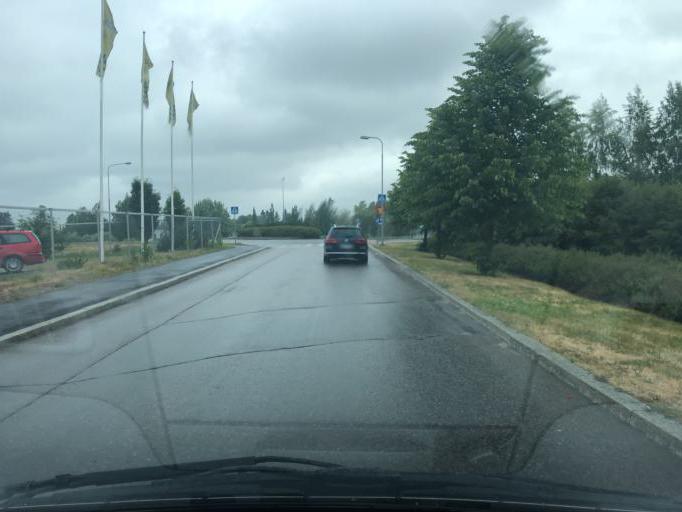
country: FI
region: Uusimaa
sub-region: Helsinki
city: Vantaa
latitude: 60.2867
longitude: 25.0160
